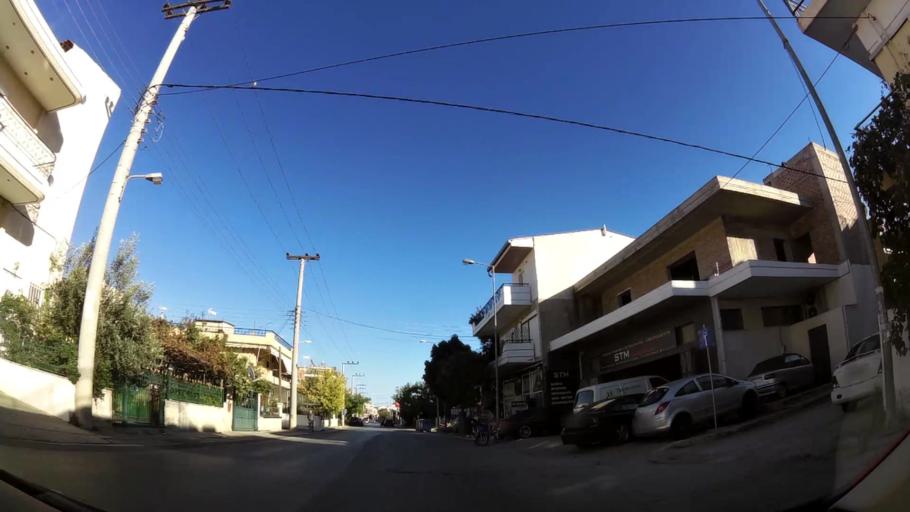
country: GR
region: Attica
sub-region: Nomarchia Anatolikis Attikis
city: Acharnes
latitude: 38.0839
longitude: 23.7266
